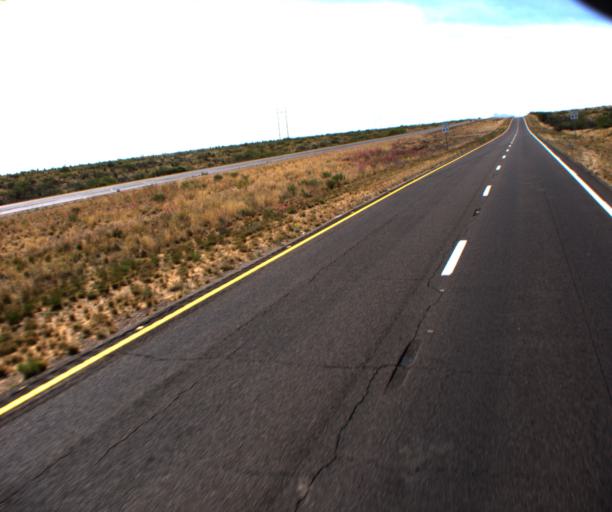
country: US
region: Arizona
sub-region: Graham County
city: Swift Trail Junction
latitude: 32.5403
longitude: -109.6762
